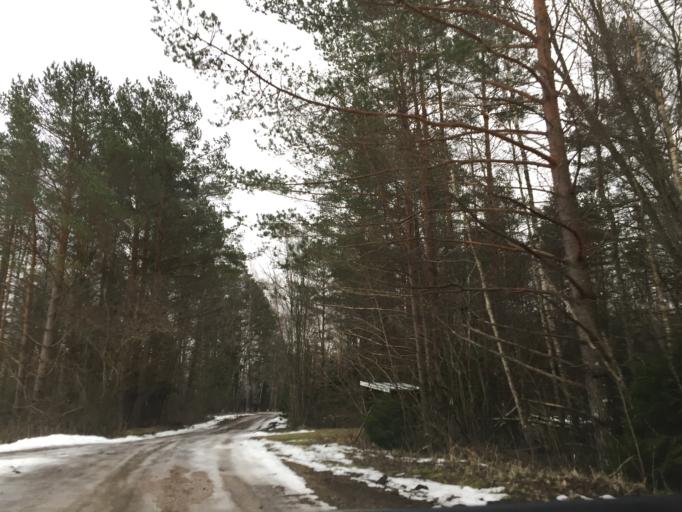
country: EE
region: Saare
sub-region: Kuressaare linn
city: Kuressaare
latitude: 58.4783
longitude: 22.2520
